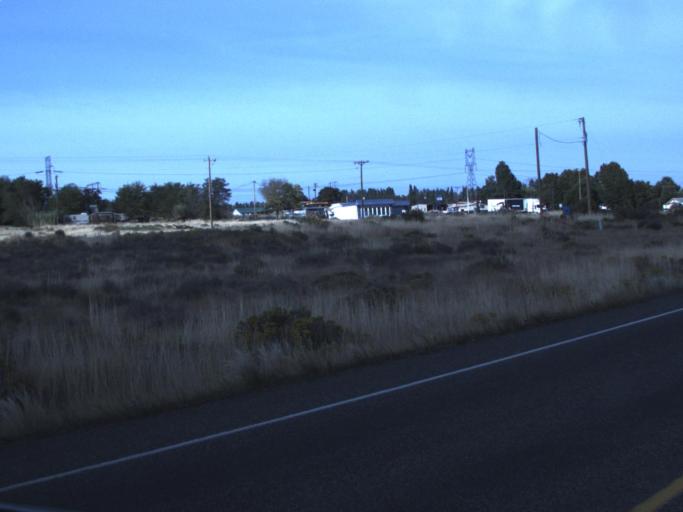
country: US
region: Oregon
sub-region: Morrow County
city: Irrigon
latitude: 45.9363
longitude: -119.6047
